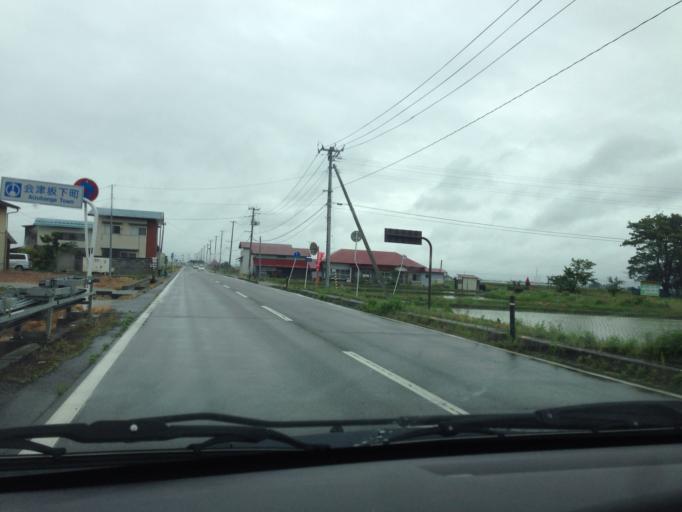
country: JP
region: Fukushima
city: Kitakata
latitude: 37.5320
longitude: 139.8341
